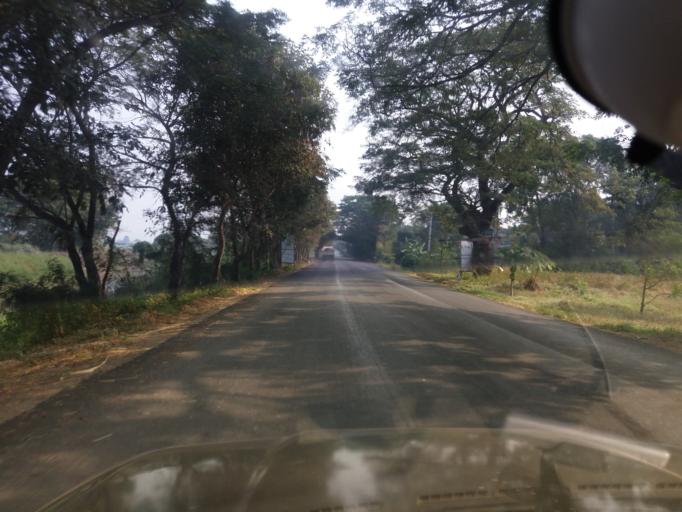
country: TH
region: Sing Buri
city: Bang Racham
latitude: 14.9044
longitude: 100.2267
